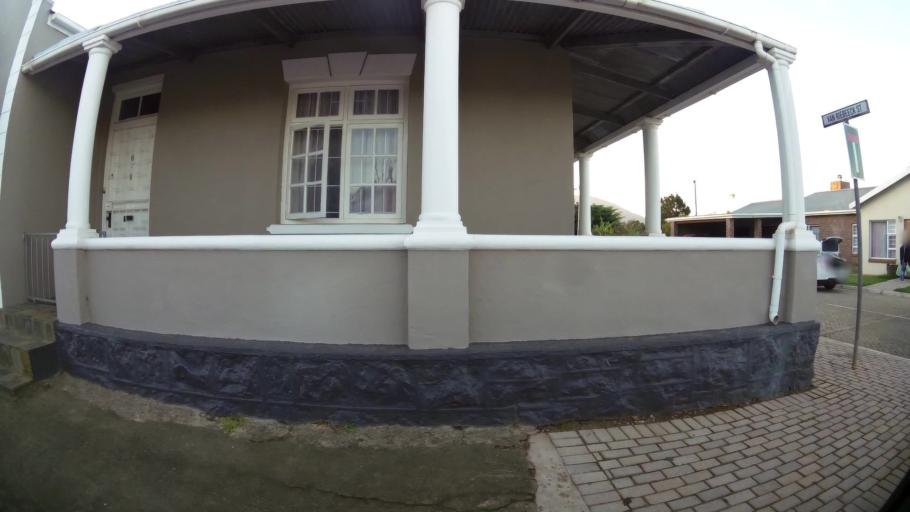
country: ZA
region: Western Cape
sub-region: Eden District Municipality
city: Riversdale
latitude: -34.0879
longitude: 21.2610
